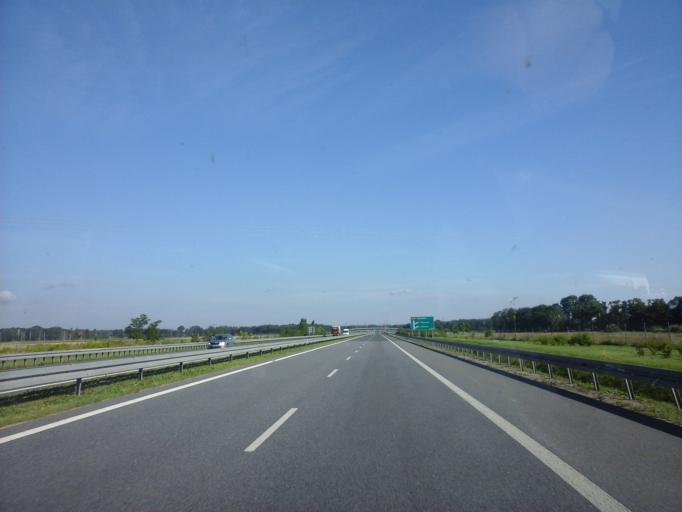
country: PL
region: West Pomeranian Voivodeship
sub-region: Powiat stargardzki
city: Kobylanka
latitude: 53.3372
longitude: 14.9564
